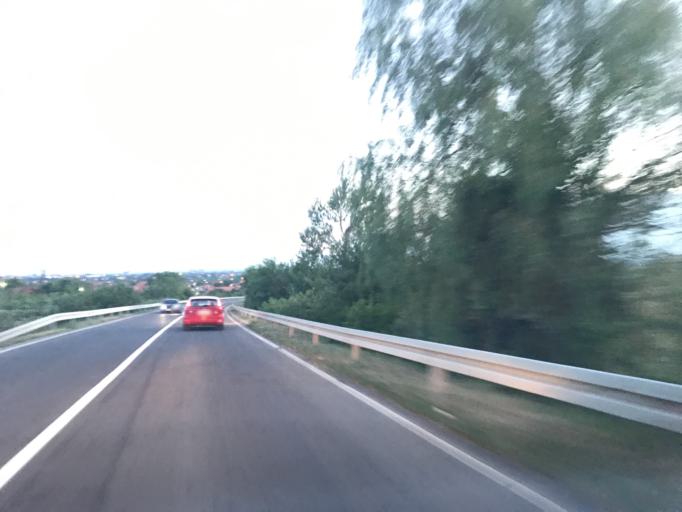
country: RS
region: Central Serbia
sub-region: Branicevski Okrug
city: Pozarevac
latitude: 44.6525
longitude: 21.1927
